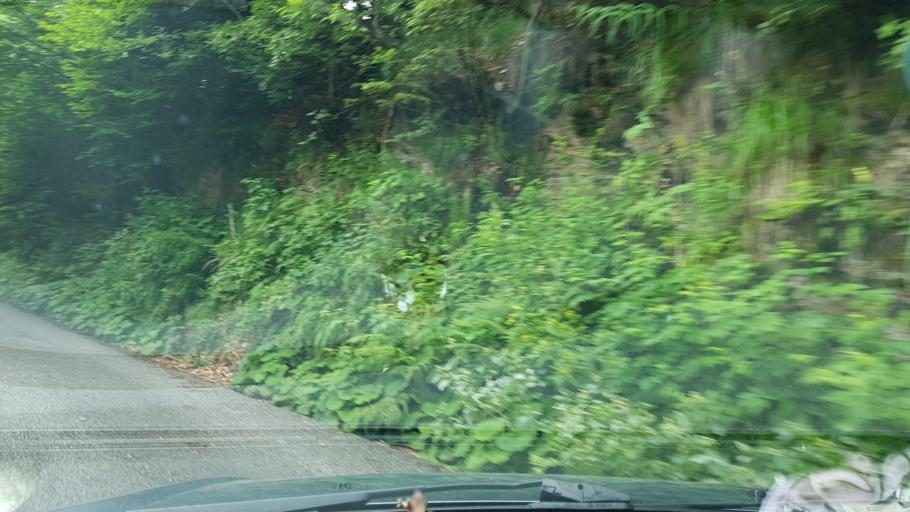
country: IT
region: Friuli Venezia Giulia
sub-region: Provincia di Udine
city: Cercivento
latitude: 46.5453
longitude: 12.9835
